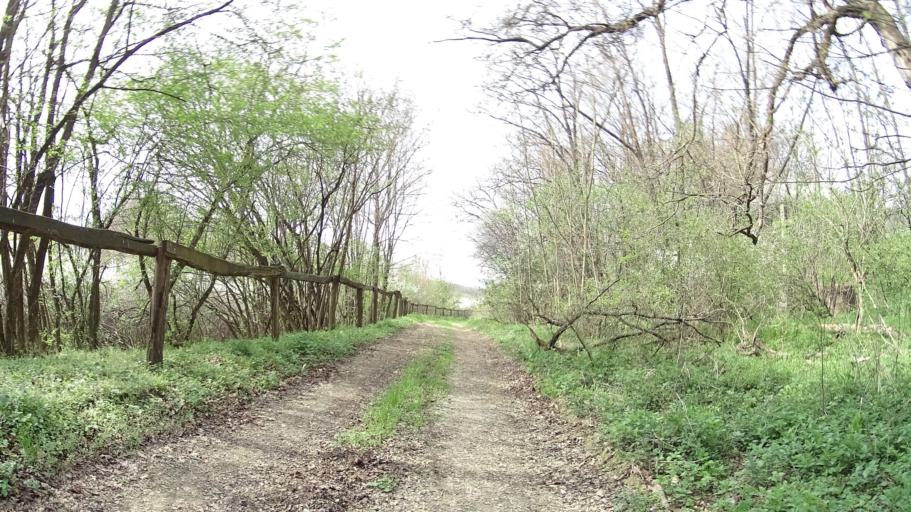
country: HU
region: Nograd
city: Retsag
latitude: 47.8785
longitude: 19.0843
